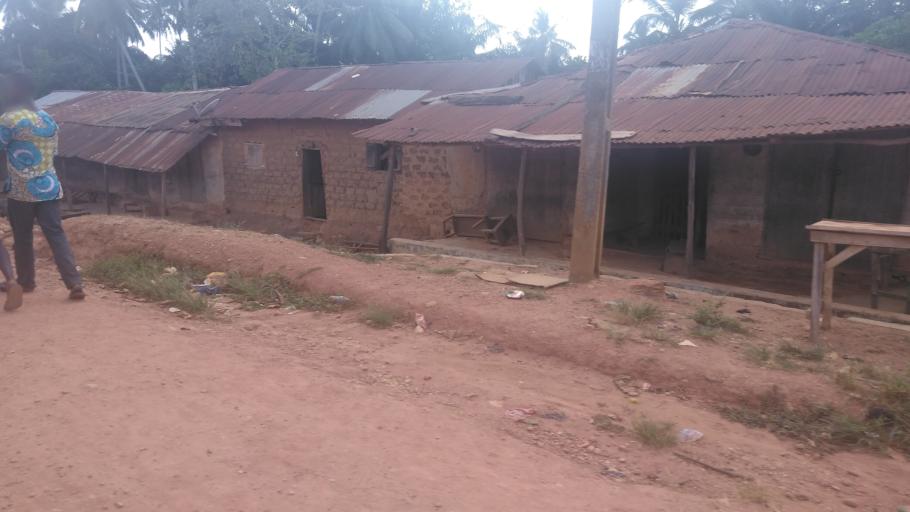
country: NG
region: Osun
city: Ifetedo
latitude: 7.0160
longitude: 4.6332
